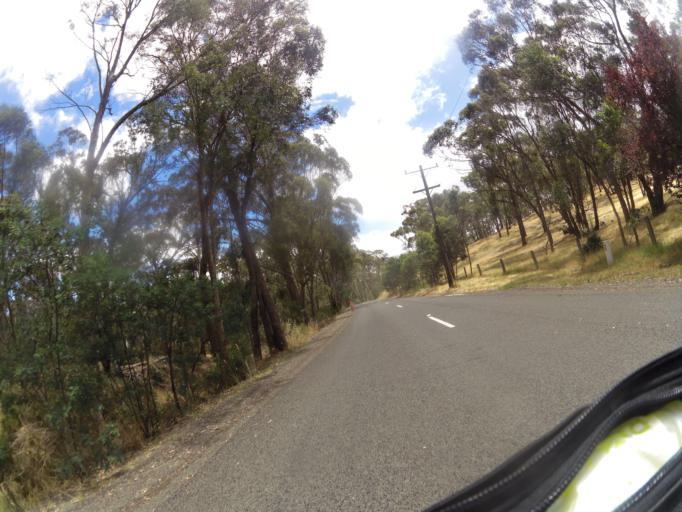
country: AU
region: Victoria
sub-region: Mount Alexander
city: Castlemaine
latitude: -37.0299
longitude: 144.2453
